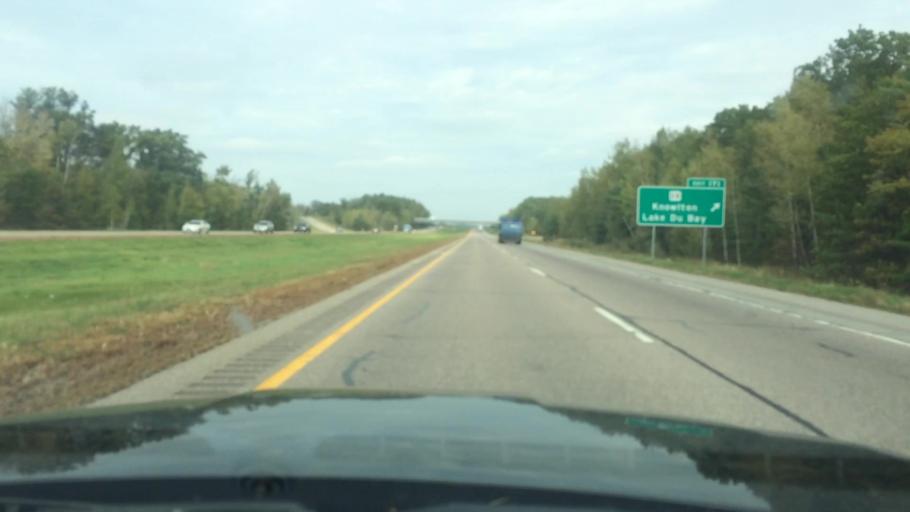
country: US
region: Wisconsin
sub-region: Marathon County
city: Mosinee
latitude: 44.6698
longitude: -89.6422
